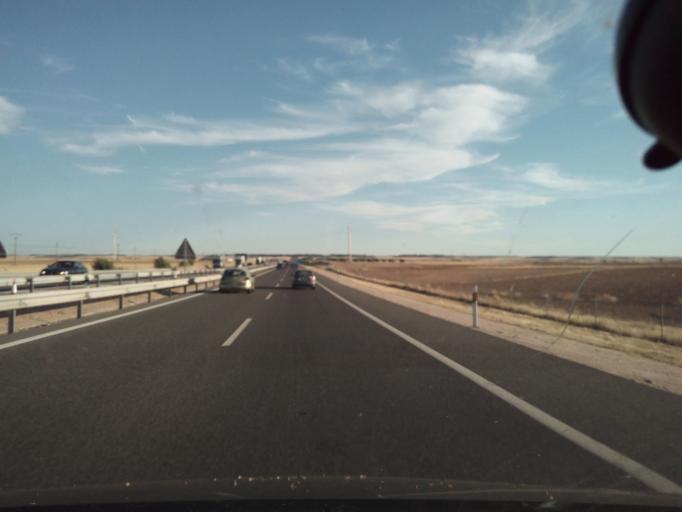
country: ES
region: Castille-La Mancha
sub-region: Province of Toledo
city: Tembleque
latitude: 39.7165
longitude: -3.4947
